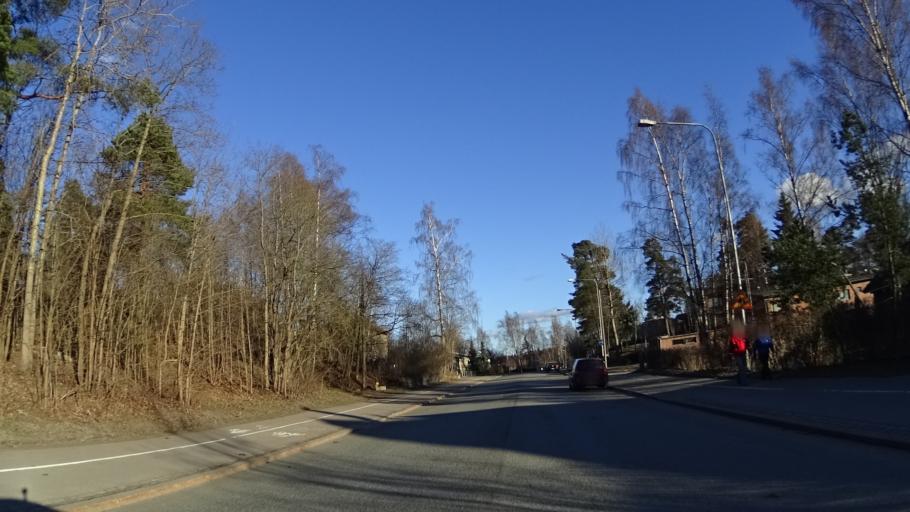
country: FI
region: Uusimaa
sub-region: Helsinki
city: Helsinki
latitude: 60.2505
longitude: 24.9568
